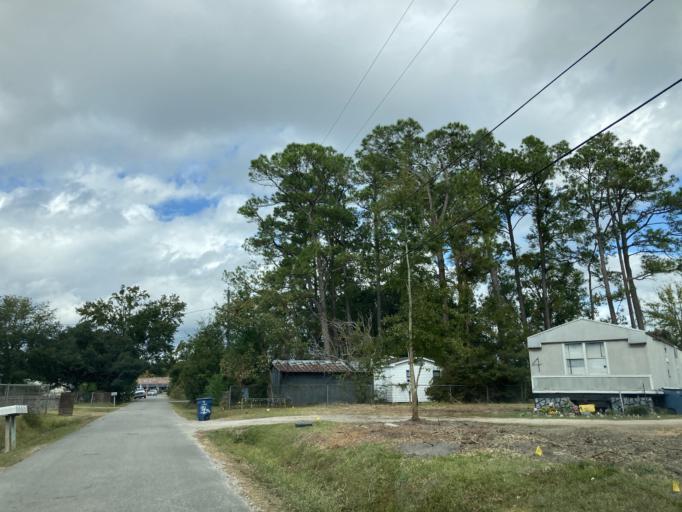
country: US
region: Mississippi
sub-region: Jackson County
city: Gulf Hills
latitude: 30.4352
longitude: -88.8324
